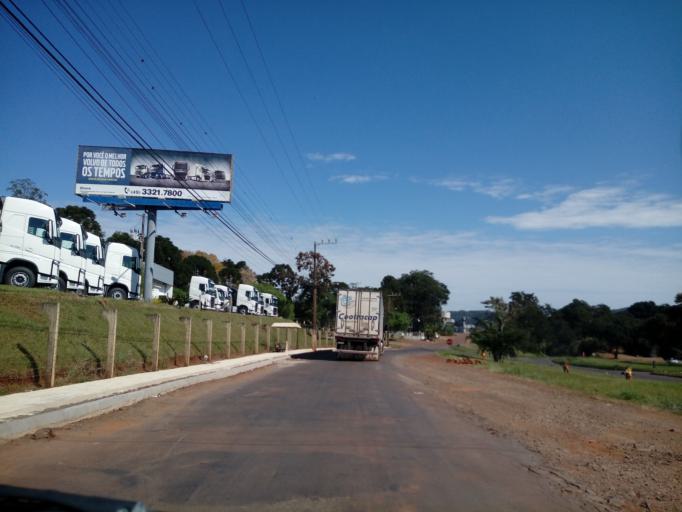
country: BR
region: Santa Catarina
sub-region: Chapeco
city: Chapeco
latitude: -27.0010
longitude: -52.6496
